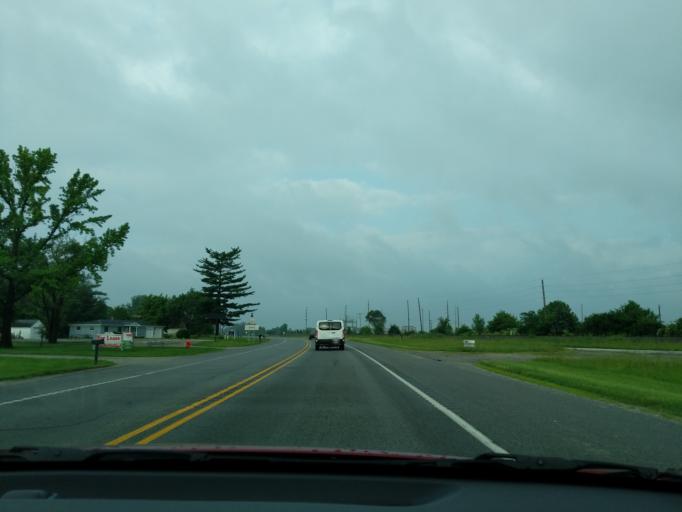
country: US
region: Indiana
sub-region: Hancock County
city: Fortville
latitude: 39.9279
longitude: -85.8586
